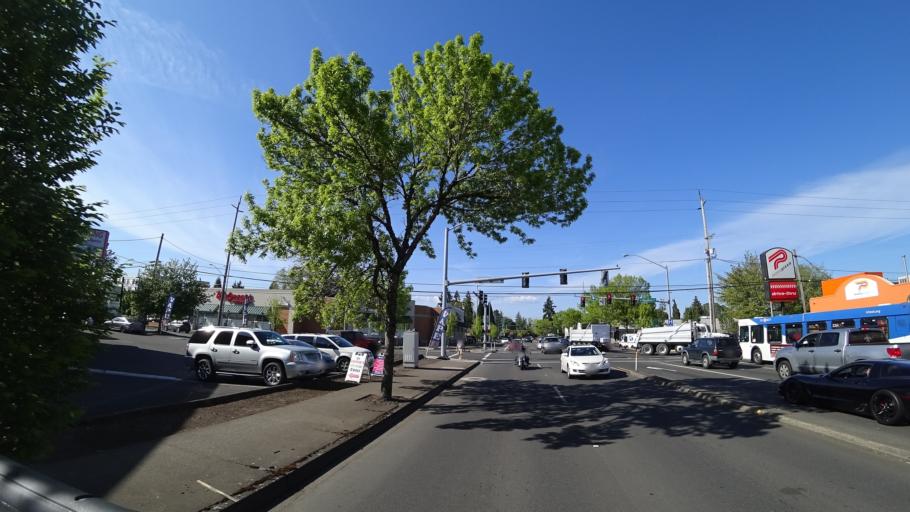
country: US
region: Oregon
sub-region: Washington County
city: Hillsboro
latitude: 45.5196
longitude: -122.9740
